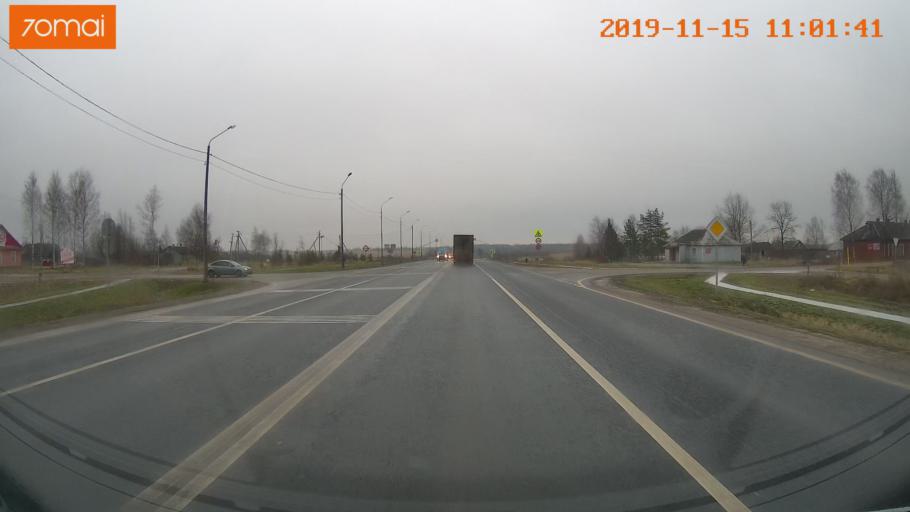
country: RU
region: Vologda
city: Chebsara
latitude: 59.1319
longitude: 38.9254
